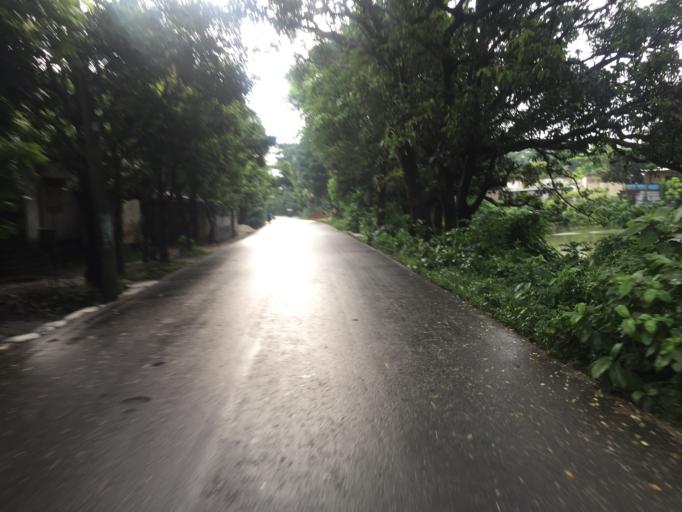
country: BD
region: Dhaka
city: Narayanganj
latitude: 23.5477
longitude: 90.4897
